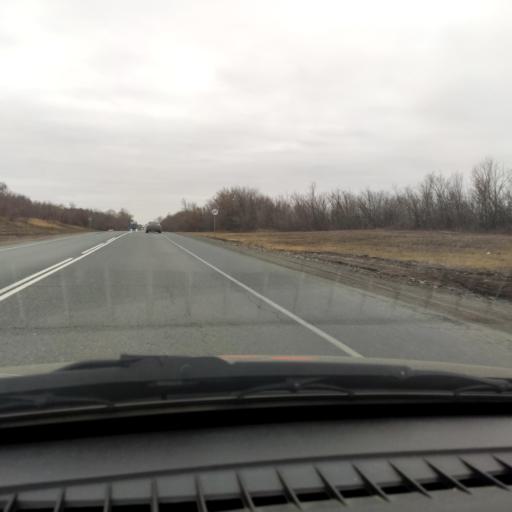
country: RU
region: Samara
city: Zhigulevsk
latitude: 53.3570
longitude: 49.4563
